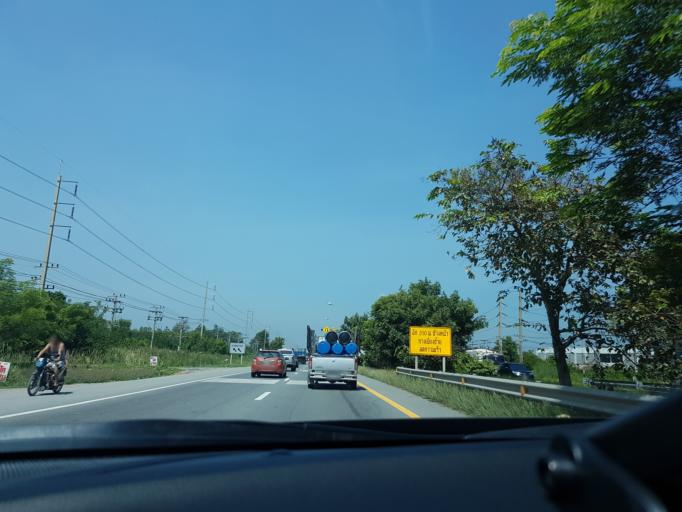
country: TH
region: Sara Buri
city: Saraburi
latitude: 14.5149
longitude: 100.8978
